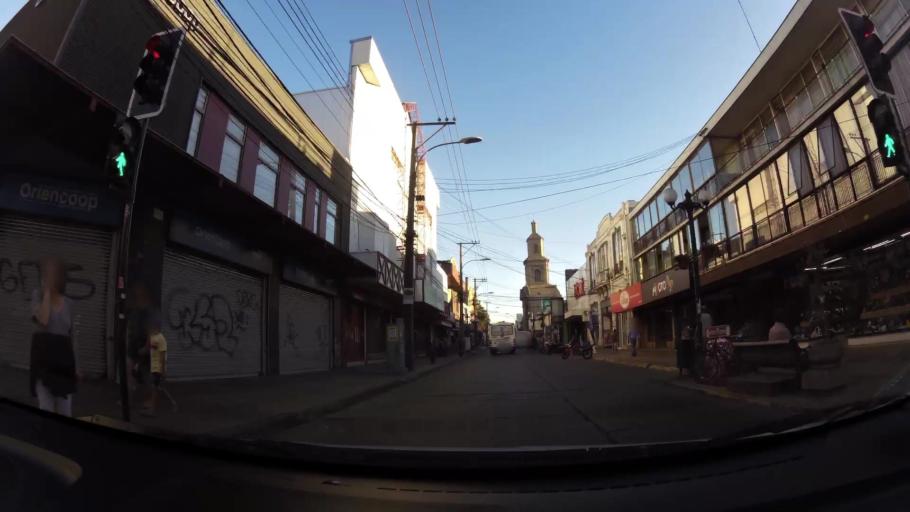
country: CL
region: Maule
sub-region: Provincia de Curico
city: Curico
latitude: -34.9838
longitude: -71.2403
